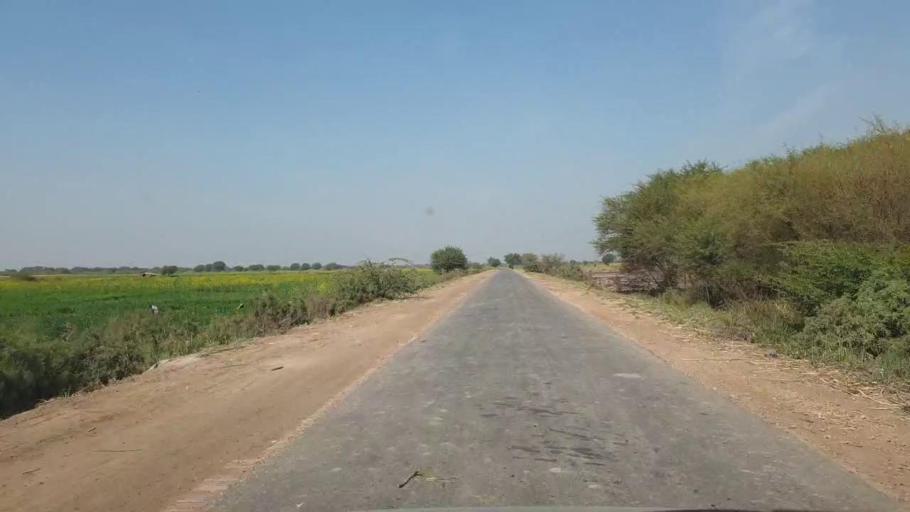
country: PK
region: Sindh
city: Chambar
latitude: 25.3154
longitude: 68.8177
